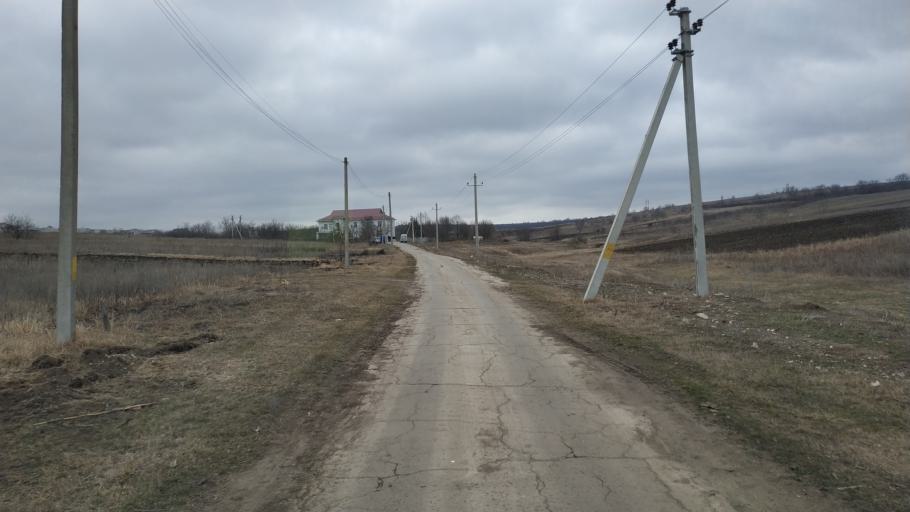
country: MD
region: Laloveni
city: Ialoveni
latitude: 46.9414
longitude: 28.7937
